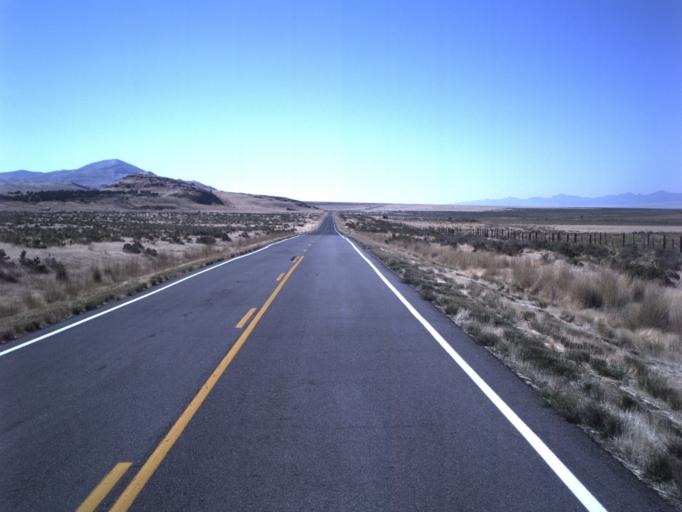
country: US
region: Utah
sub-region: Tooele County
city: Grantsville
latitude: 40.6246
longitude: -112.6984
